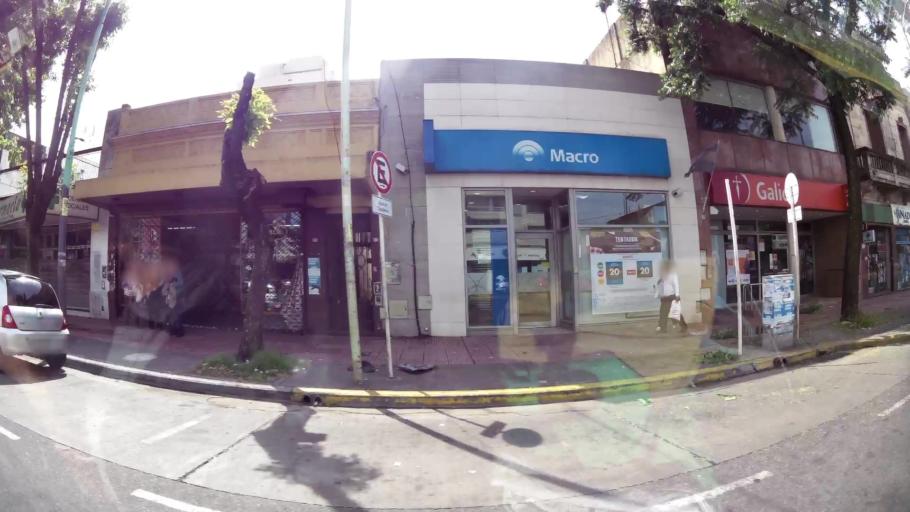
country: AR
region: Buenos Aires F.D.
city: Villa Lugano
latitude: -34.6519
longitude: -58.5029
